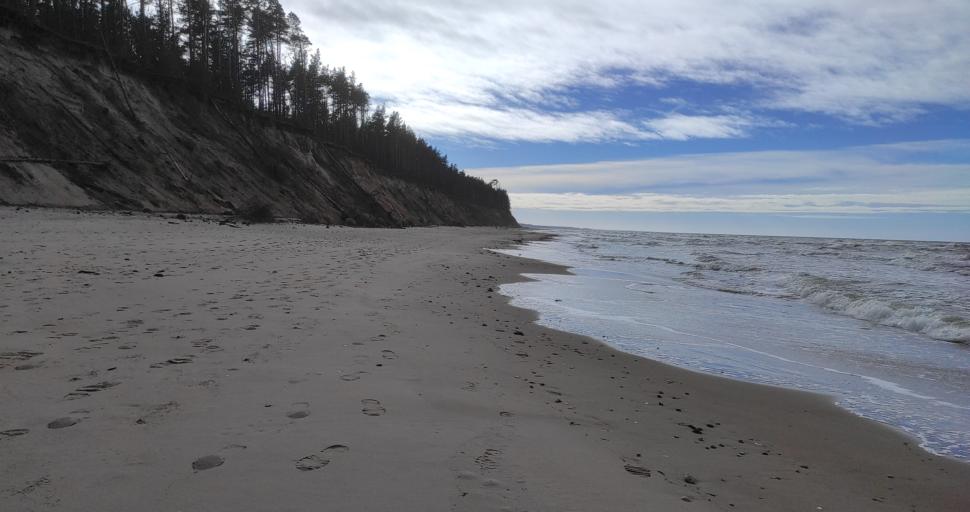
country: LV
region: Alsunga
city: Alsunga
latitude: 57.0241
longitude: 21.3921
